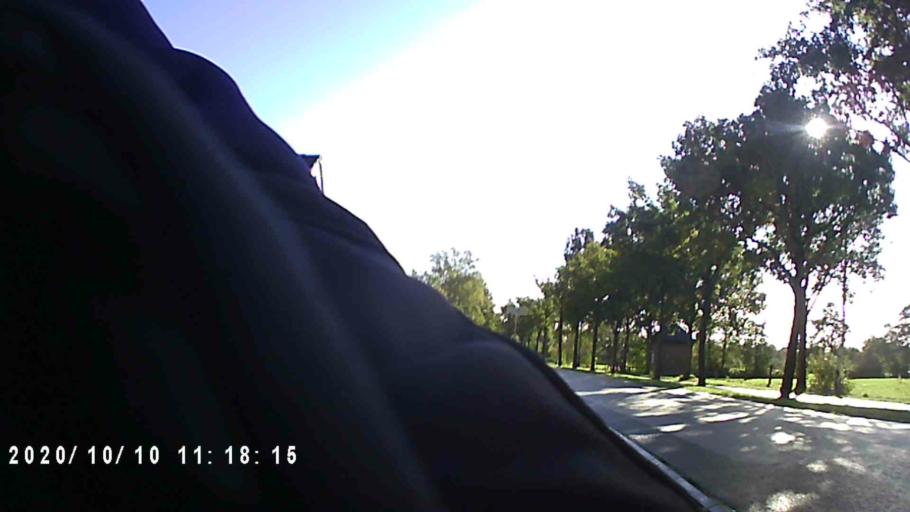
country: NL
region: Friesland
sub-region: Gemeente Smallingerland
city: Drachtstercompagnie
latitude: 53.0944
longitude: 6.1970
